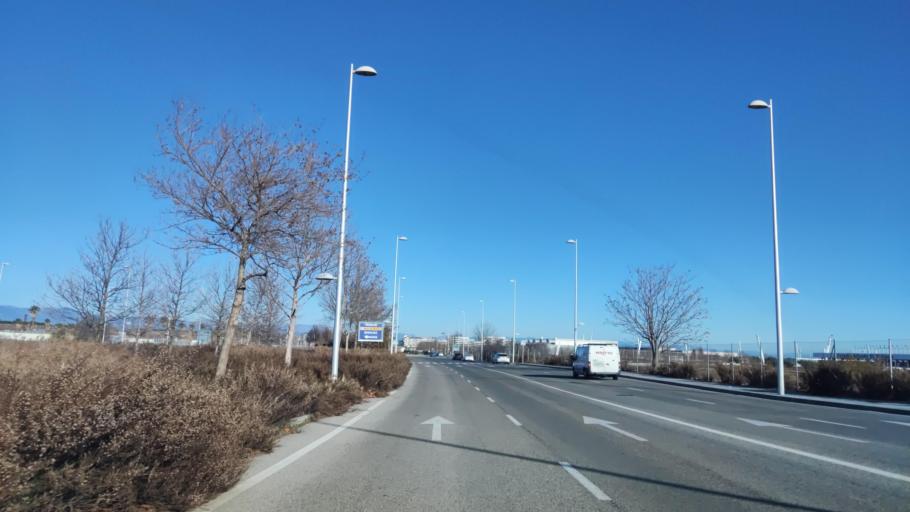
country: ES
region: Madrid
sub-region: Provincia de Madrid
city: Hortaleza
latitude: 40.4741
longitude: -3.6179
